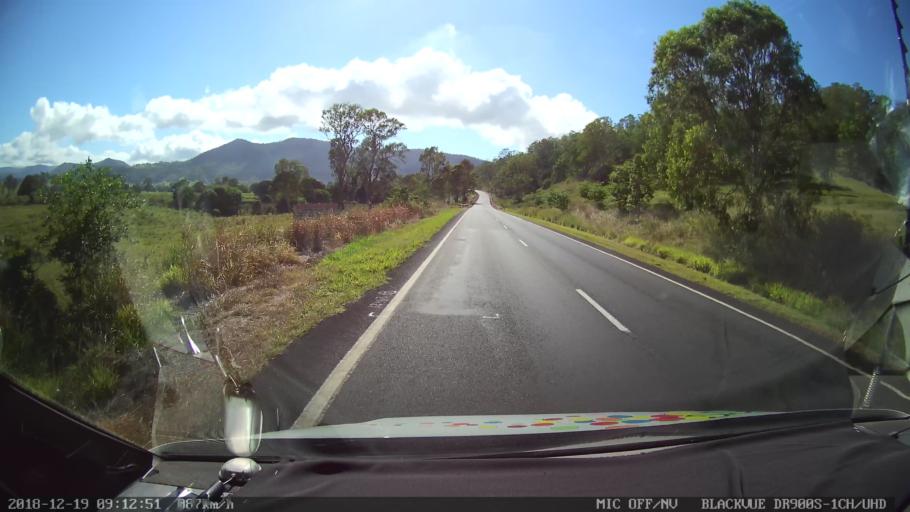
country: AU
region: New South Wales
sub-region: Kyogle
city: Kyogle
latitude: -28.5002
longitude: 152.9547
